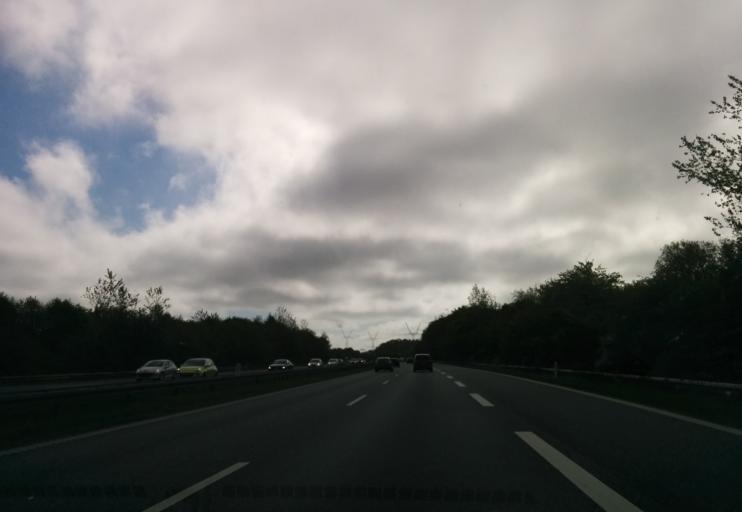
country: DK
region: South Denmark
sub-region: Assens Kommune
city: Arup
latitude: 55.4121
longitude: 10.0460
